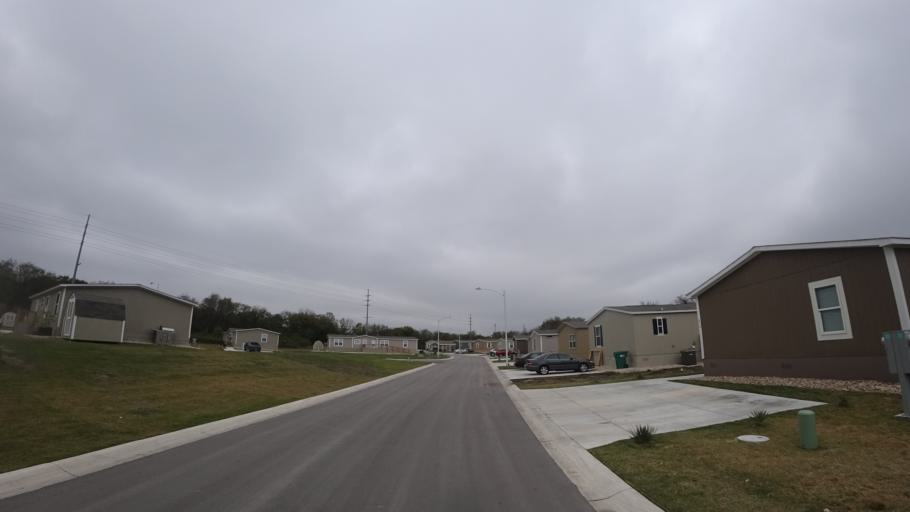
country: US
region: Texas
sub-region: Travis County
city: Pflugerville
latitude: 30.3916
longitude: -97.6378
